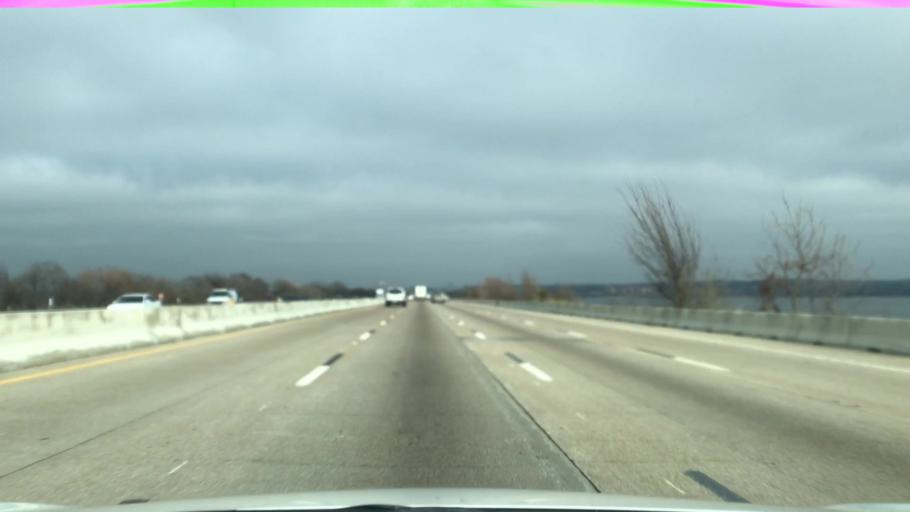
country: US
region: Texas
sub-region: Rockwall County
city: Heath
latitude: 32.8830
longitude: -96.5042
